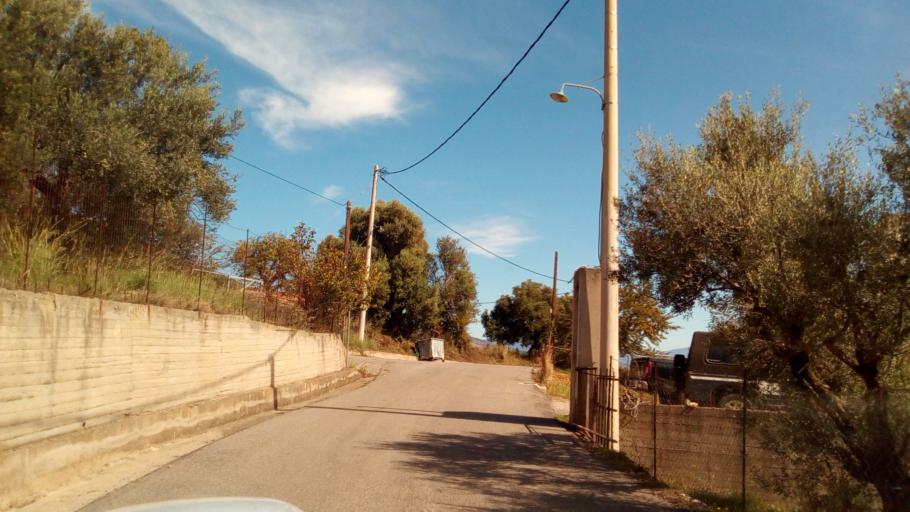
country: GR
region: West Greece
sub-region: Nomos Aitolias kai Akarnanias
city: Antirrio
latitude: 38.3600
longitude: 21.7533
